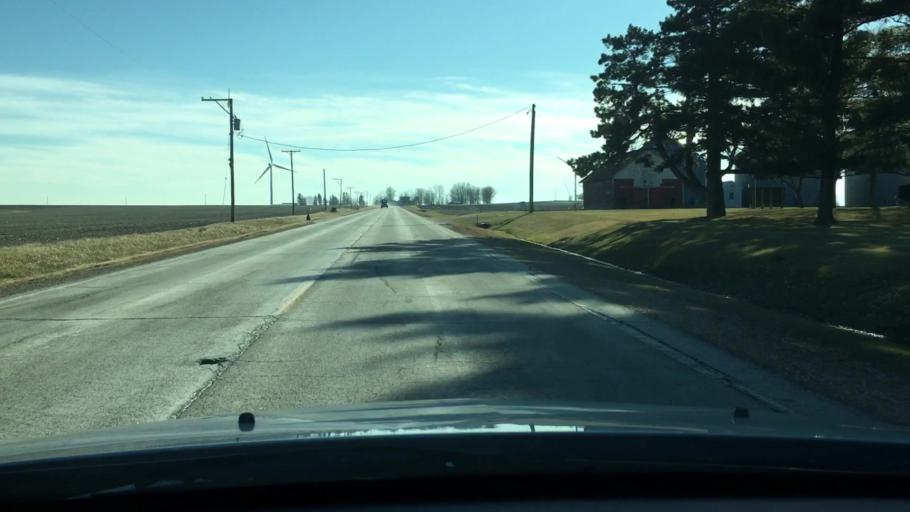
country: US
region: Illinois
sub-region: LaSalle County
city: Mendota
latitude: 41.6336
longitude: -89.1295
